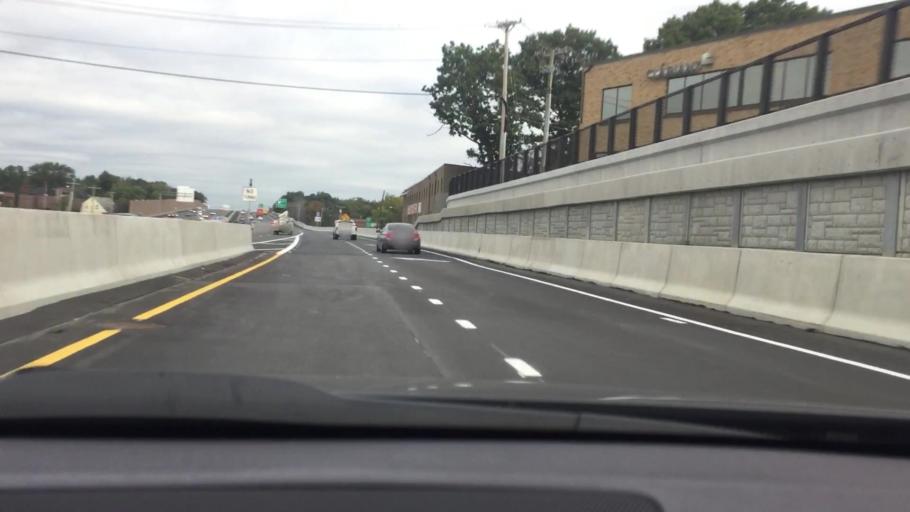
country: US
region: Massachusetts
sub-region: Norfolk County
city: Needham
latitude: 42.3055
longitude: -71.2258
